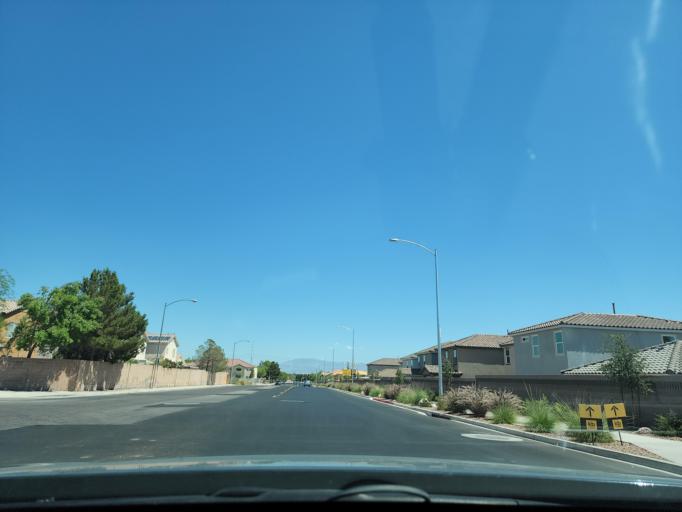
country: US
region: Nevada
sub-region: Clark County
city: Spring Valley
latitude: 36.0822
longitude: -115.2518
